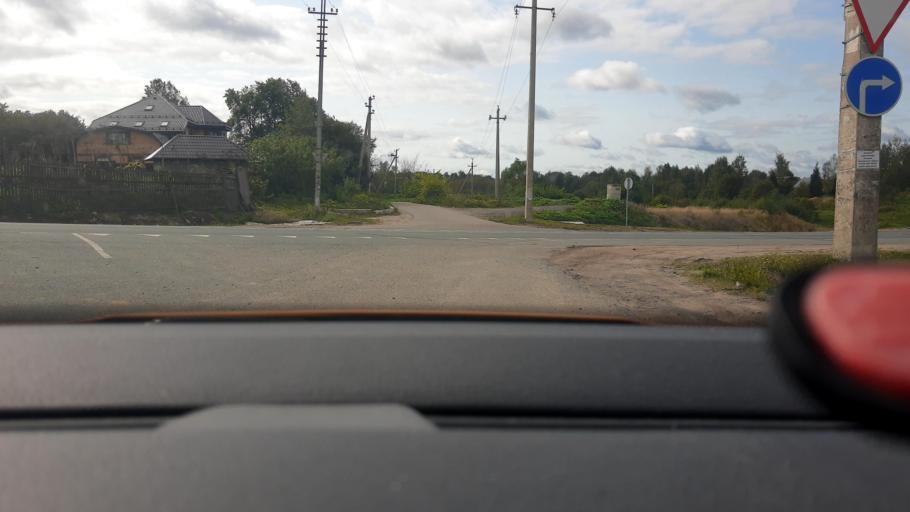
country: RU
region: Moskovskaya
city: Krasnoarmeysk
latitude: 56.0781
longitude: 38.0314
